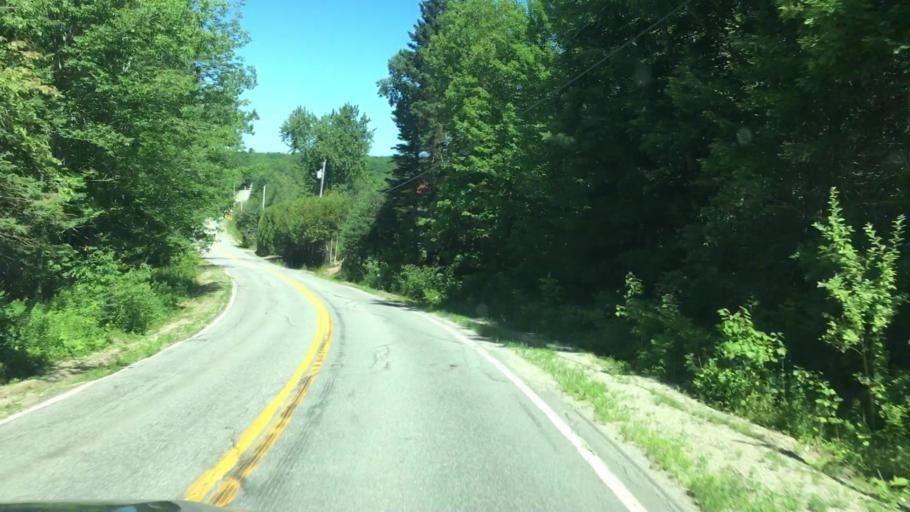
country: US
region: Maine
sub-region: Hancock County
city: Penobscot
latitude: 44.4236
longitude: -68.7068
